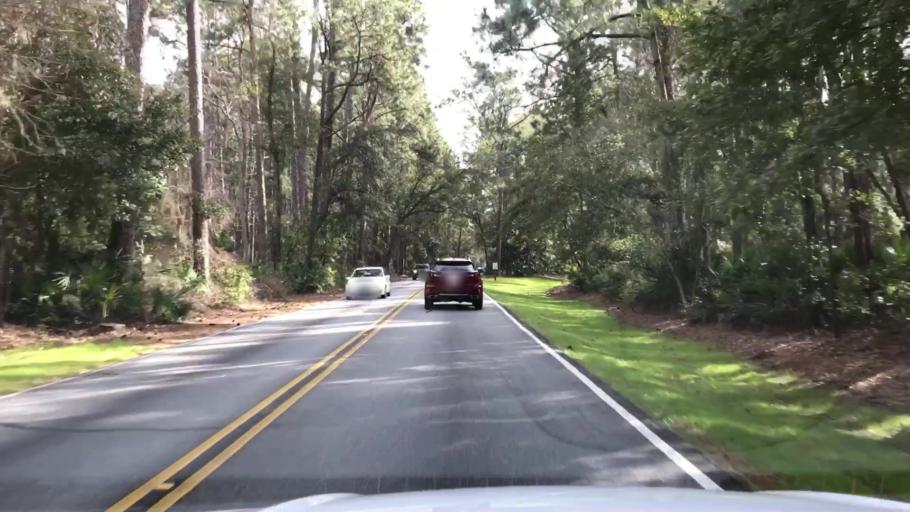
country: US
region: South Carolina
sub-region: Beaufort County
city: Hilton Head Island
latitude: 32.2287
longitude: -80.7246
